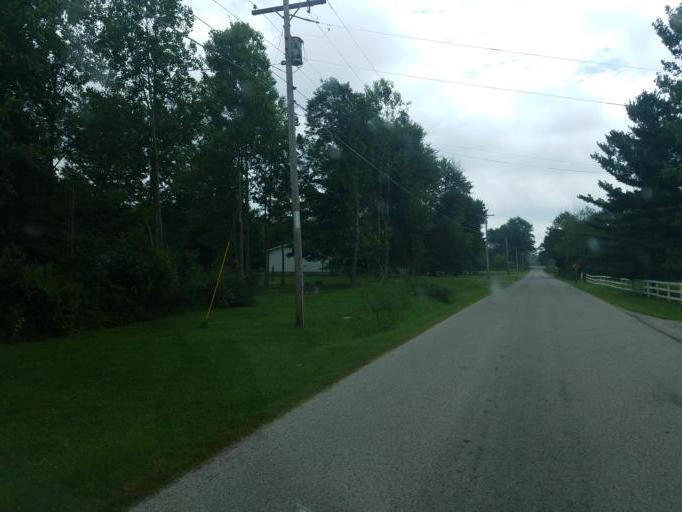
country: US
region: Ohio
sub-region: Morrow County
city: Mount Gilead
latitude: 40.4775
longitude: -82.7859
